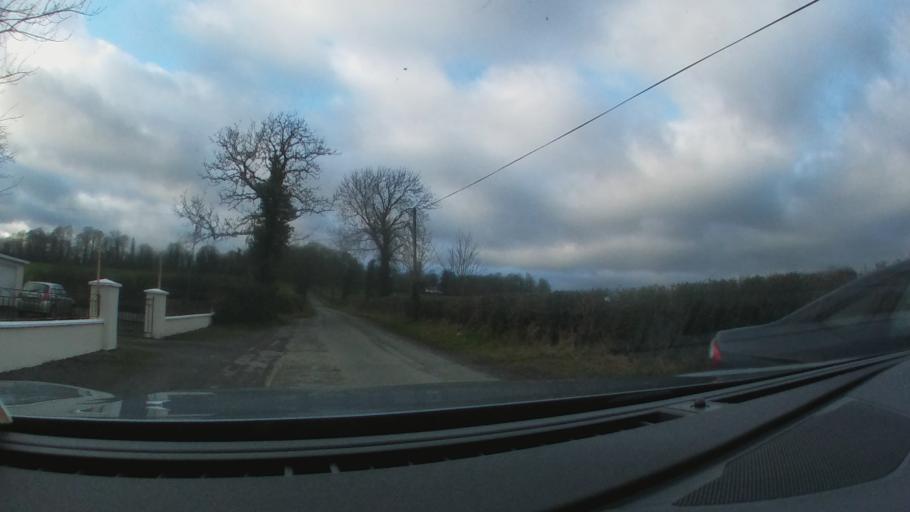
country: IE
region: Leinster
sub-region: Kilkenny
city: Thomastown
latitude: 52.5586
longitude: -7.1312
